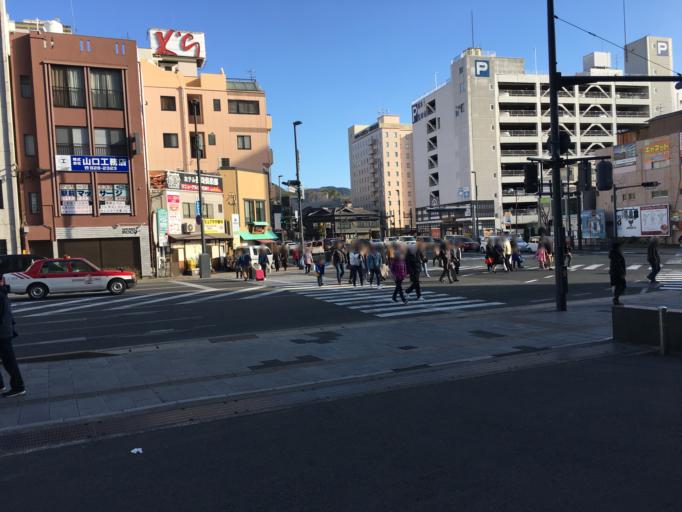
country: JP
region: Nagasaki
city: Nagasaki-shi
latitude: 32.7465
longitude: 129.8708
